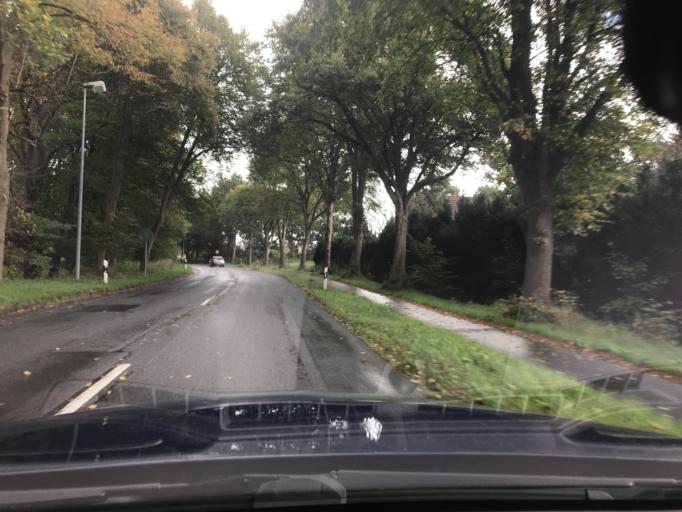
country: DE
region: Lower Saxony
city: Stade
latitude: 53.5784
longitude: 9.4710
